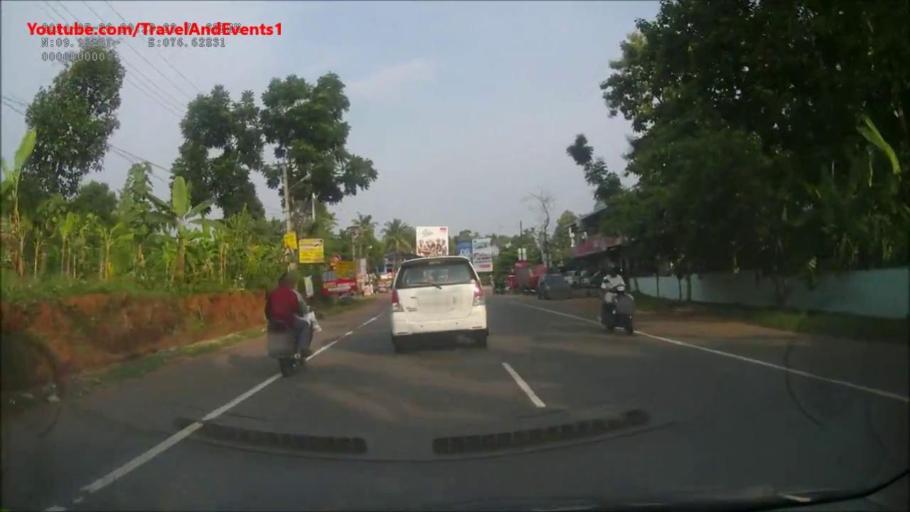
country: IN
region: Kerala
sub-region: Ernakulam
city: Muvattupula
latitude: 9.9467
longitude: 76.6345
